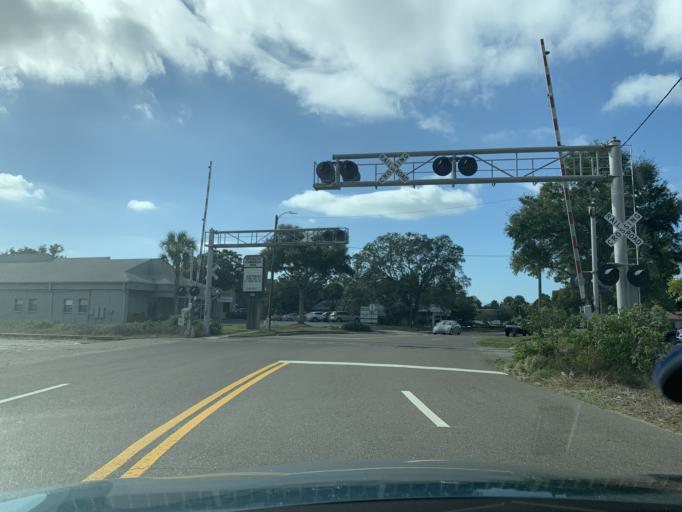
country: US
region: Florida
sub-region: Pinellas County
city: Belleair
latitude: 27.9483
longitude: -82.7970
